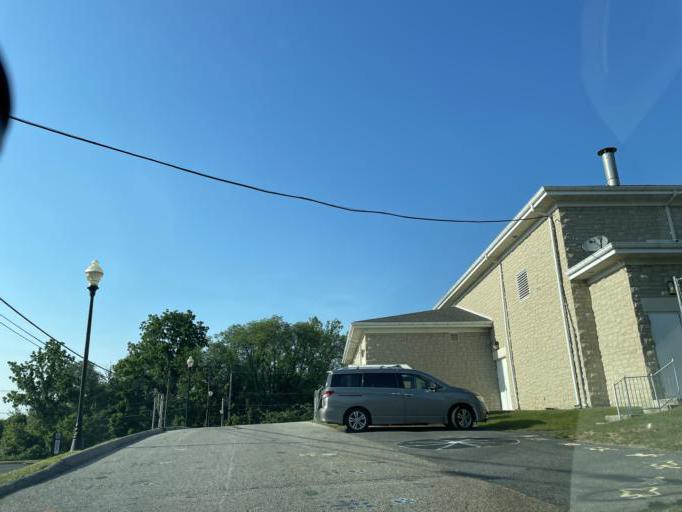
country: US
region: Maryland
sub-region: Baltimore County
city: Cockeysville
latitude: 39.4629
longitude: -76.6401
